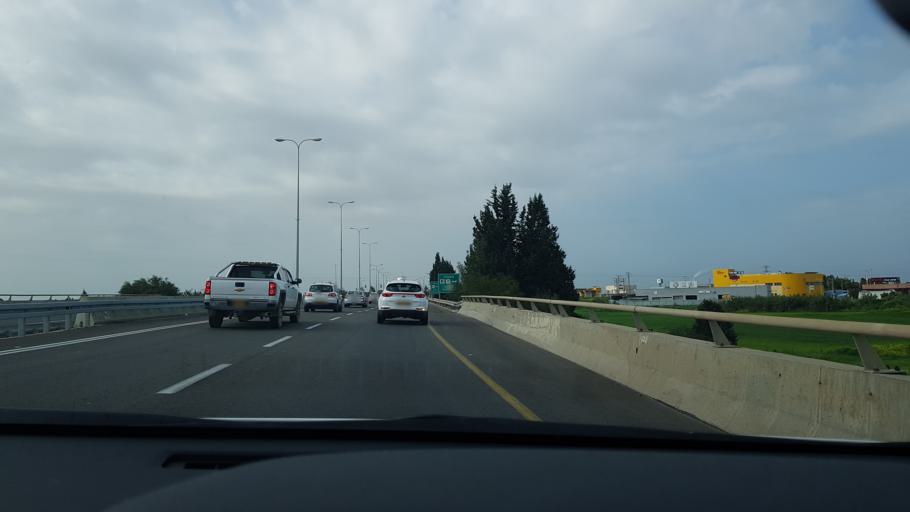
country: IL
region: Southern District
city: Ashqelon
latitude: 31.6610
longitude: 34.6052
